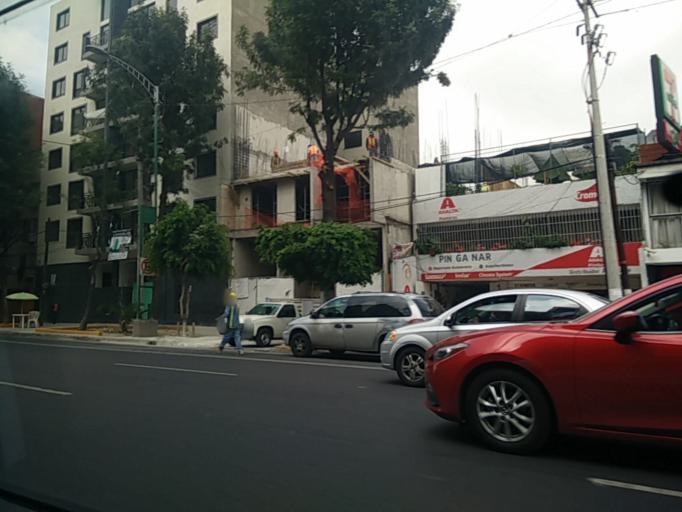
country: MX
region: Mexico City
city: Colonia del Valle
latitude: 19.3764
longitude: -99.1598
